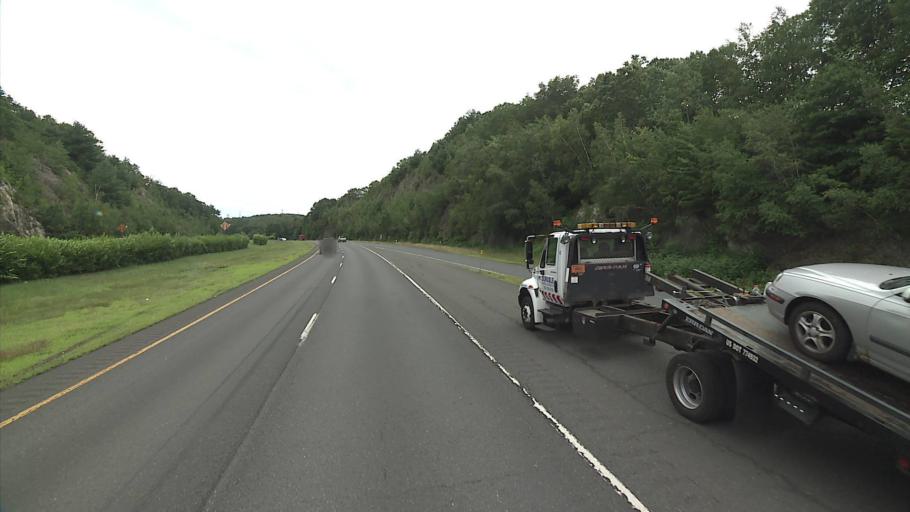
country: US
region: Connecticut
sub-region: Litchfield County
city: Oakville
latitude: 41.6022
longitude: -73.0665
